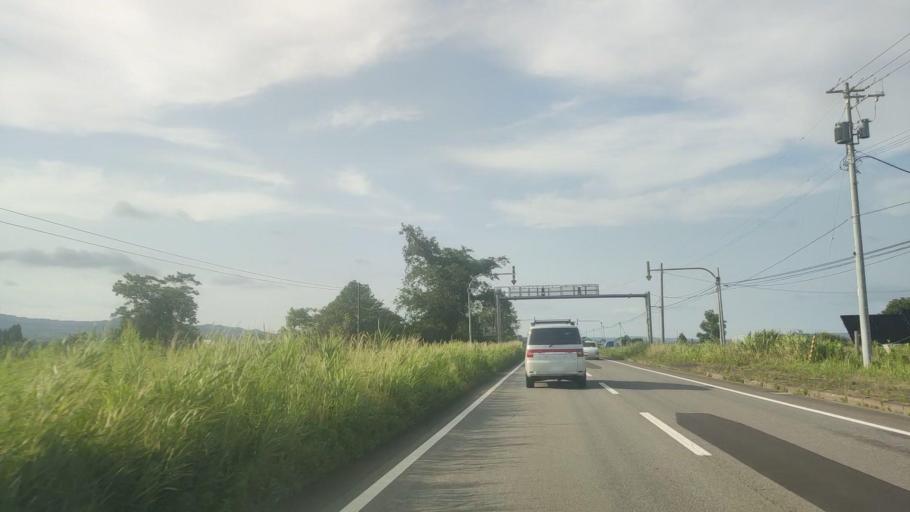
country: JP
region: Hokkaido
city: Chitose
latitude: 42.9590
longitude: 141.7981
